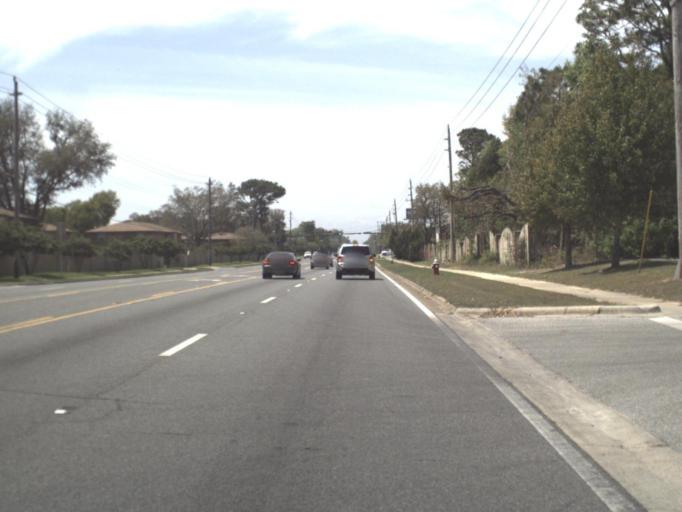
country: US
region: Florida
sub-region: Escambia County
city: West Pensacola
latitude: 30.4607
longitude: -87.2769
